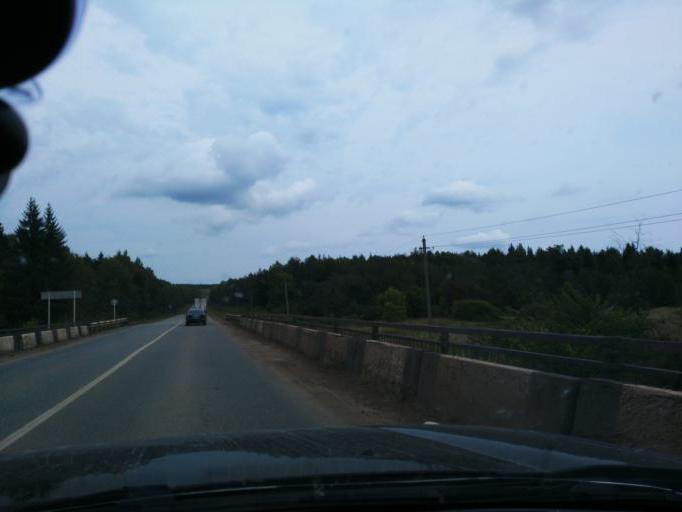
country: RU
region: Perm
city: Kuyeda
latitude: 56.4559
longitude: 55.6207
